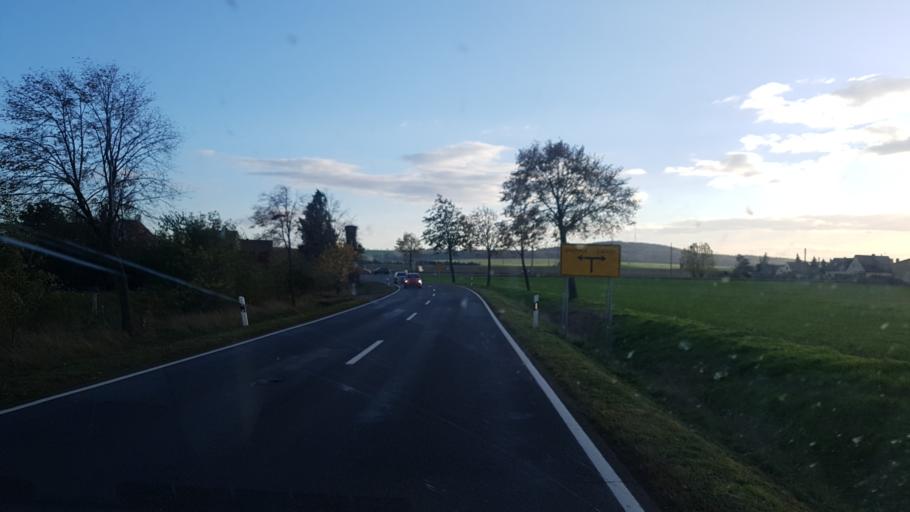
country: DE
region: Saxony
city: Dahlen
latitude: 51.3394
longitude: 13.0302
